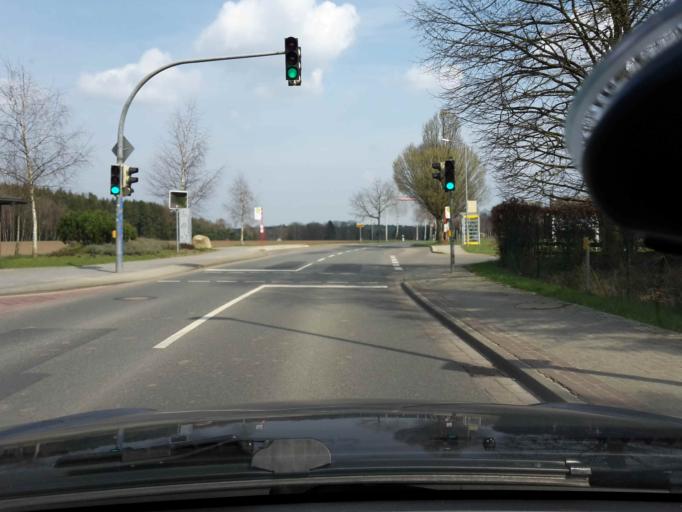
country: DE
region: Lower Saxony
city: Buchholz in der Nordheide
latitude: 53.2958
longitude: 9.8699
